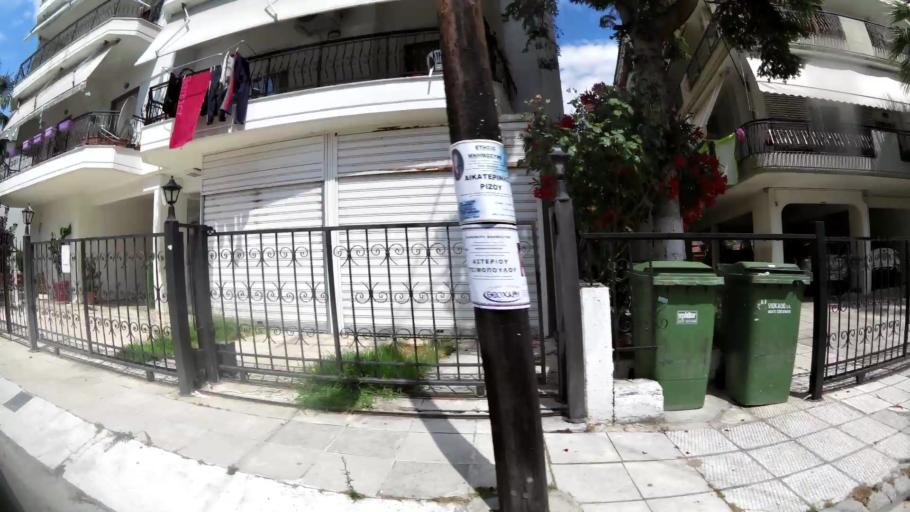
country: GR
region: Central Macedonia
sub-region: Nomos Pierias
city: Katerini
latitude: 40.2734
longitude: 22.4980
